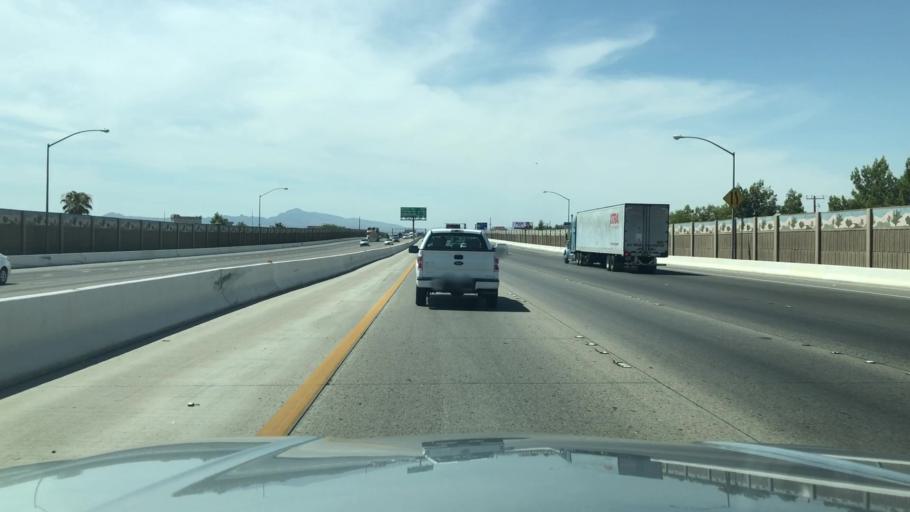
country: US
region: Nevada
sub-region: Clark County
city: Winchester
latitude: 36.1494
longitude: -115.0919
